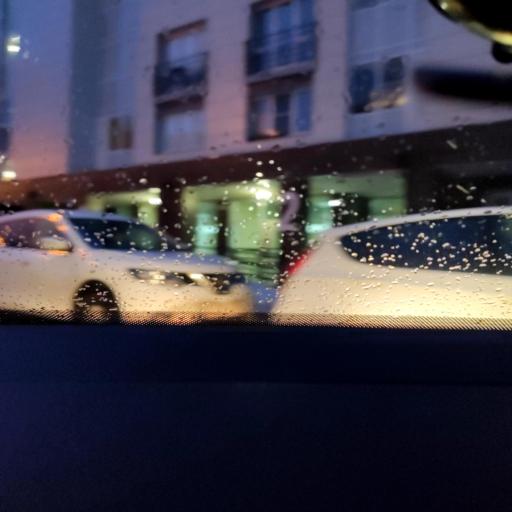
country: RU
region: Moskovskaya
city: Nakhabino
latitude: 55.8524
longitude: 37.1882
